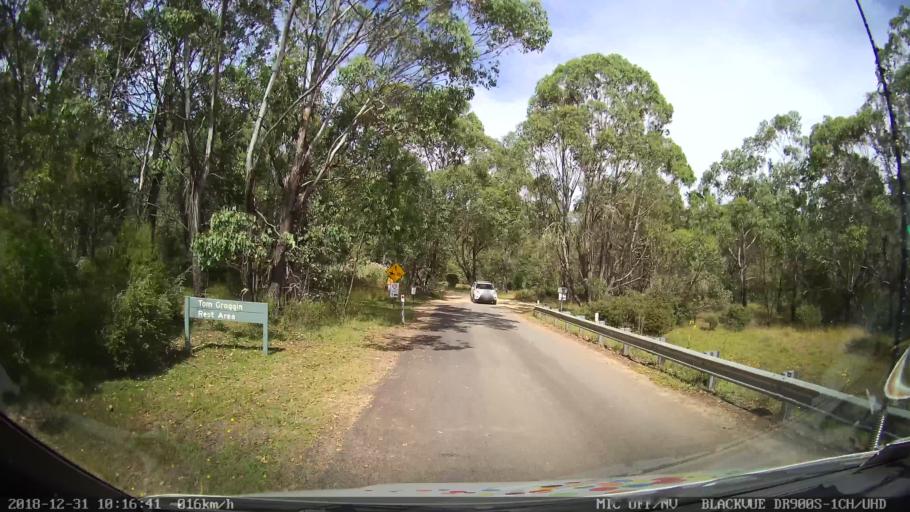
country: AU
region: New South Wales
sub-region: Snowy River
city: Jindabyne
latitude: -36.5384
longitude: 148.1353
